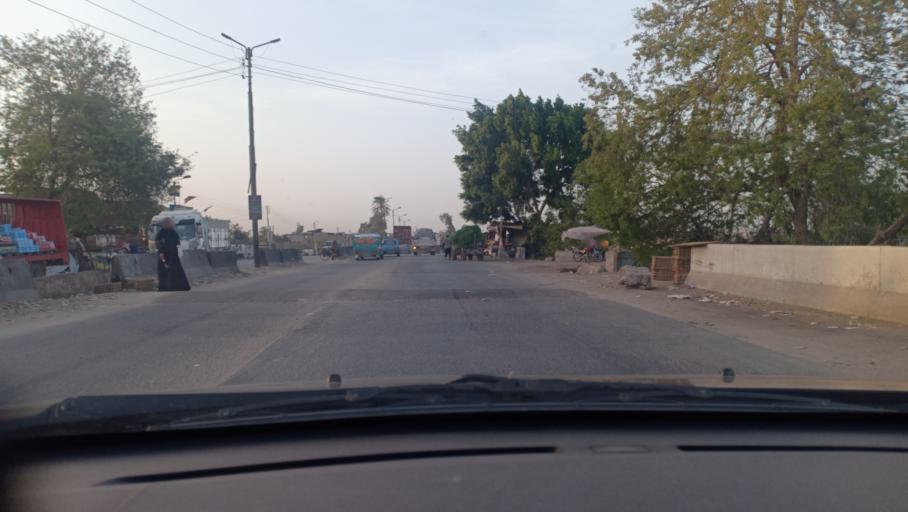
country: EG
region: Muhafazat al Gharbiyah
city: Zifta
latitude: 30.6567
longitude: 31.2841
